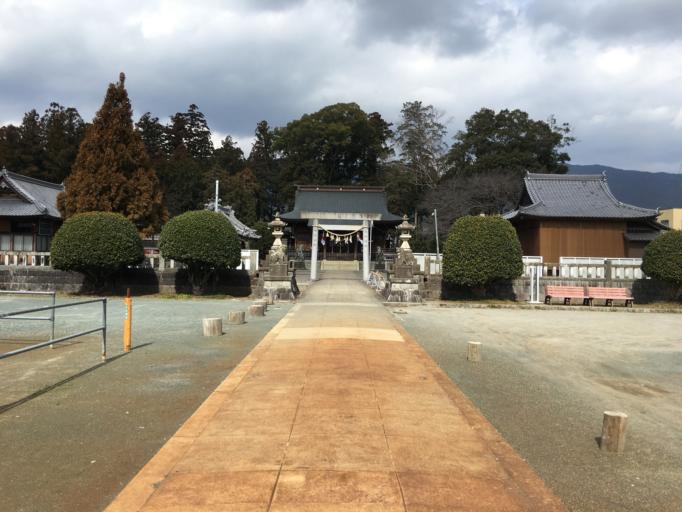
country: JP
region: Aichi
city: Shinshiro
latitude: 34.9025
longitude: 137.4939
